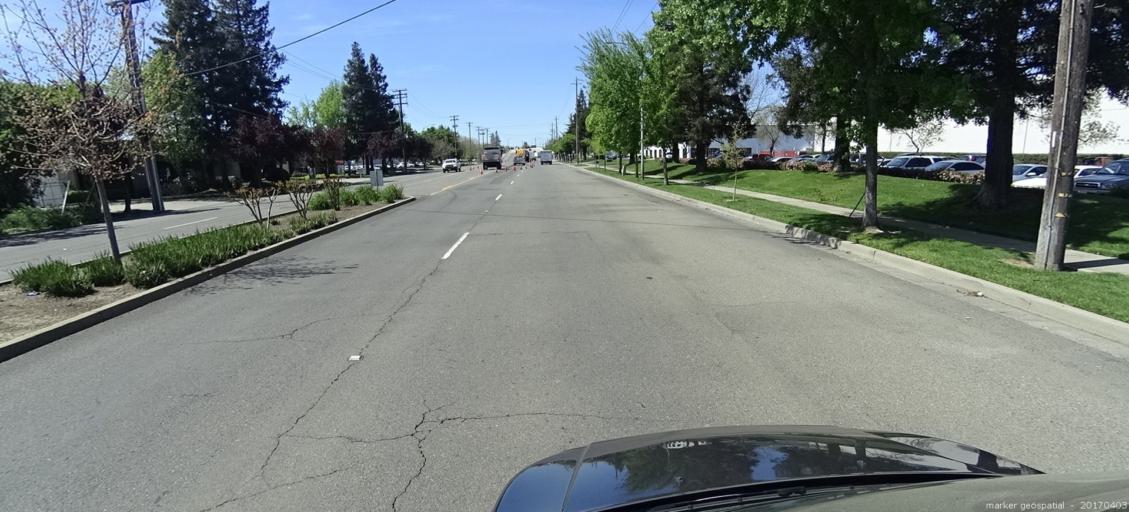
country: US
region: California
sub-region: Sacramento County
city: Rio Linda
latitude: 38.6554
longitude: -121.4680
